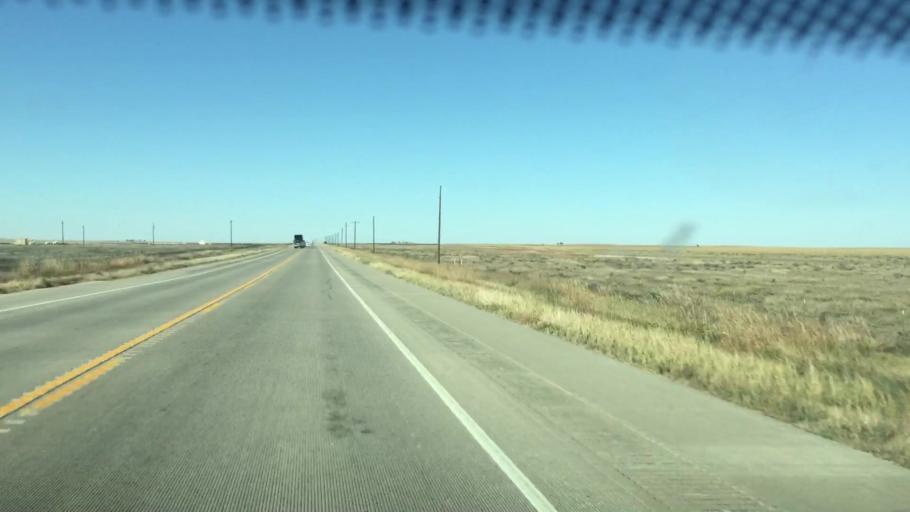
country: US
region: Colorado
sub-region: Kiowa County
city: Eads
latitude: 38.6614
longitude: -102.7858
